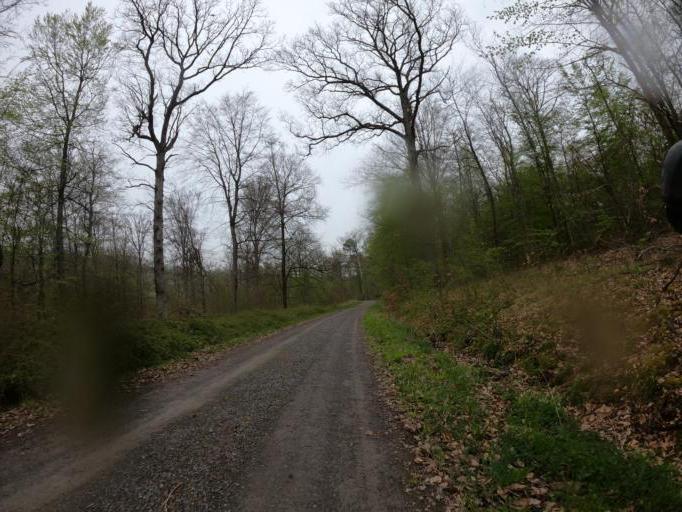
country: DE
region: Baden-Wuerttemberg
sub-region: Karlsruhe Region
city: Illingen
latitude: 48.9788
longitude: 8.8912
